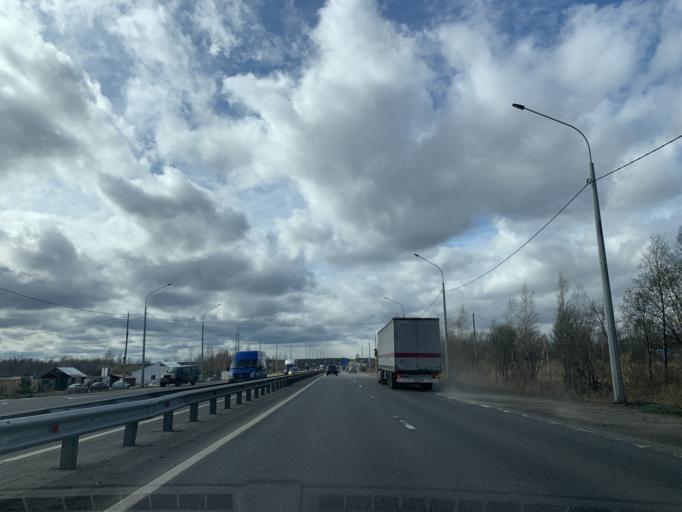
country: RU
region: Jaroslavl
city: Yaroslavl
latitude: 57.6822
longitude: 39.9170
